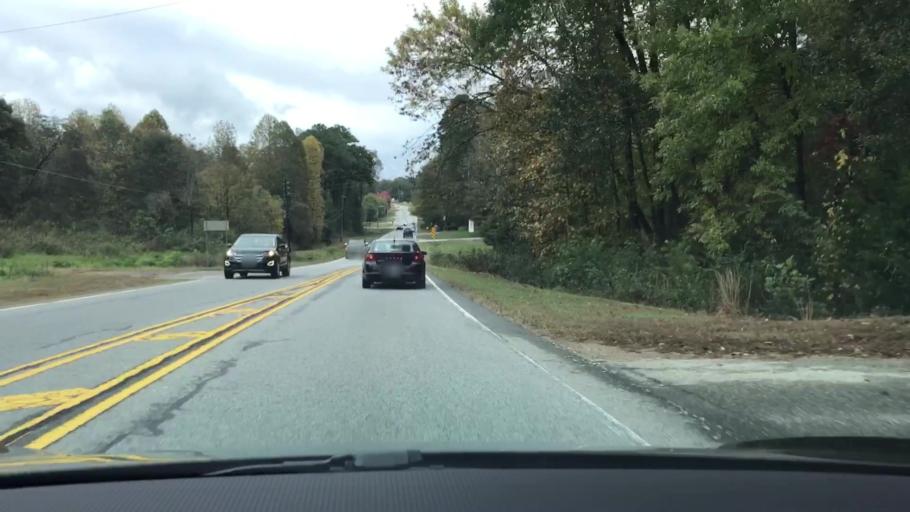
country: US
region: Georgia
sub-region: Oconee County
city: Watkinsville
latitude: 33.8693
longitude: -83.4192
